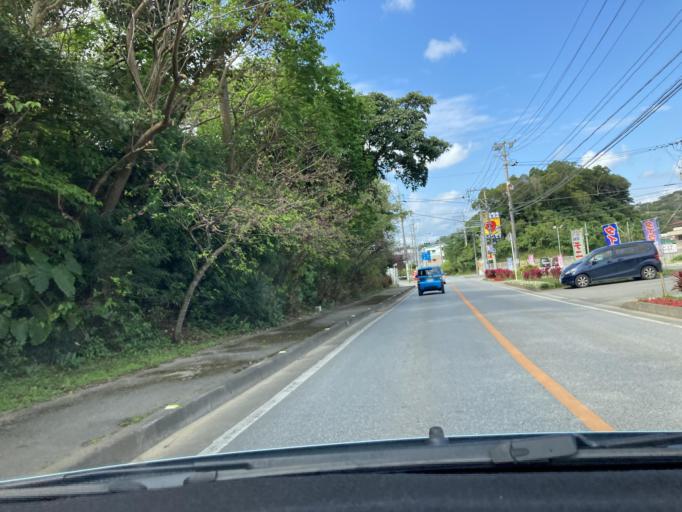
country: JP
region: Okinawa
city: Nago
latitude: 26.6565
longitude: 127.9043
